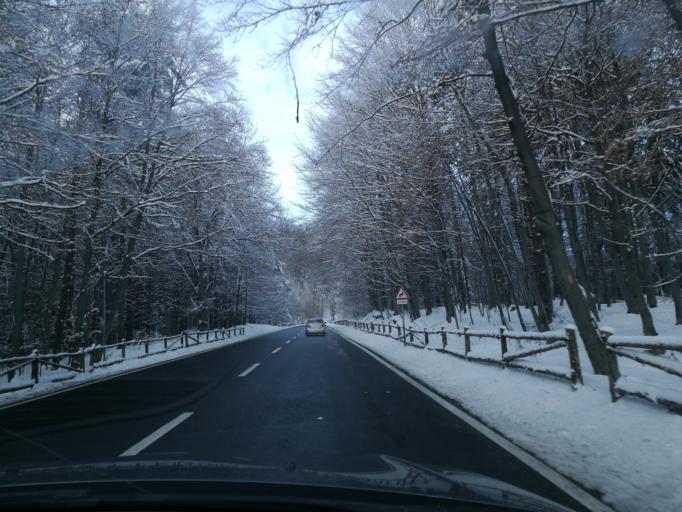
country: RO
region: Brasov
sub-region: Comuna Ghimbav
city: Ghimbav
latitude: 45.6183
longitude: 25.5442
